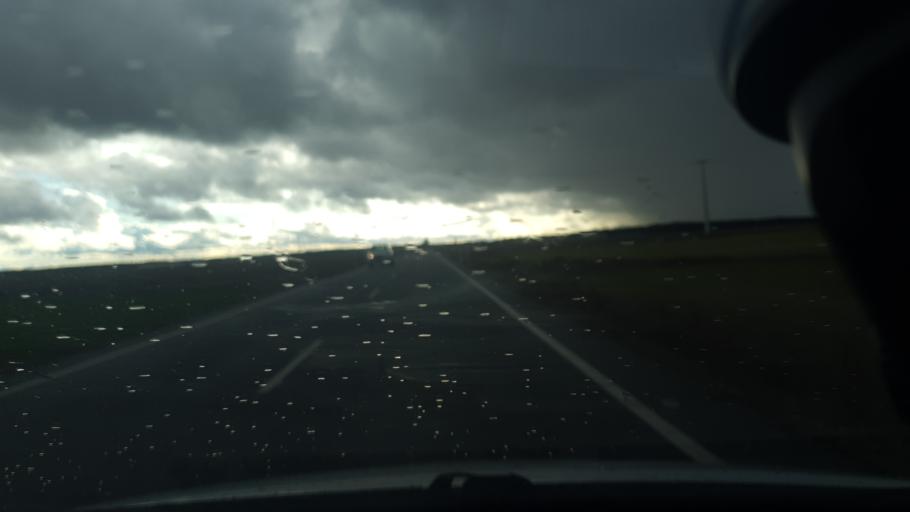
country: ES
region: Castille and Leon
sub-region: Provincia de Segovia
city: Chane
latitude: 41.3092
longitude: -4.3966
